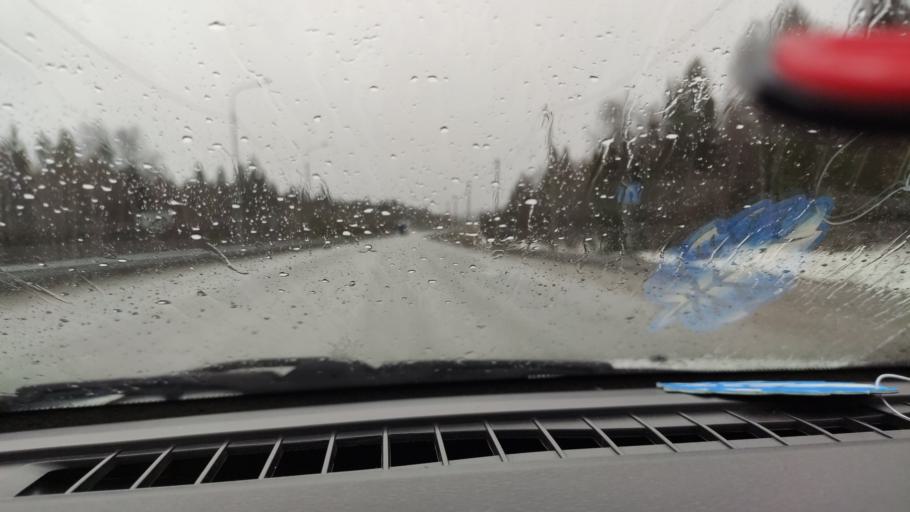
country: RU
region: Sverdlovsk
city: Arti
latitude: 56.7918
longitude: 58.4958
